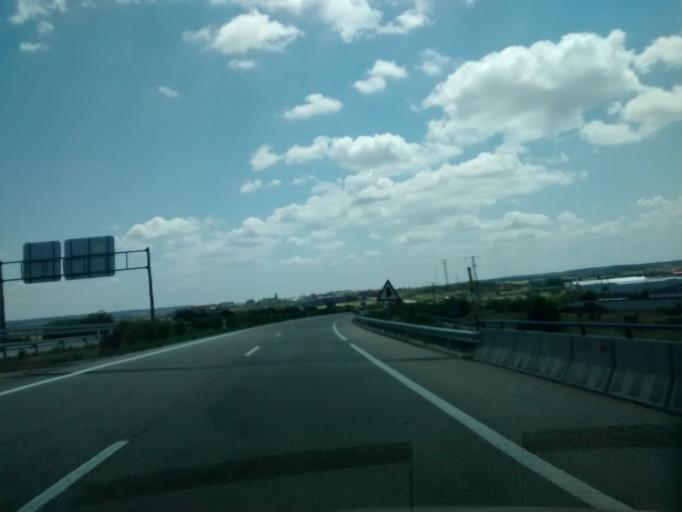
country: ES
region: Castille and Leon
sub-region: Provincia de Leon
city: Astorga
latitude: 42.4740
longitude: -6.0868
